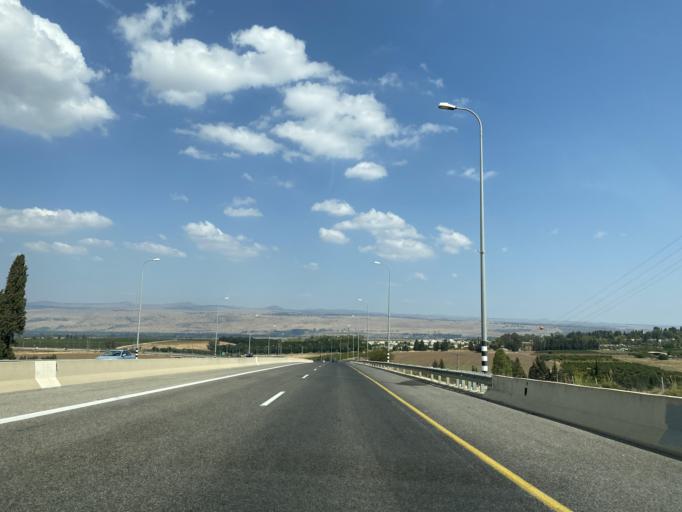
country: IL
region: Northern District
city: Rosh Pinna
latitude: 33.0280
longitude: 35.5631
